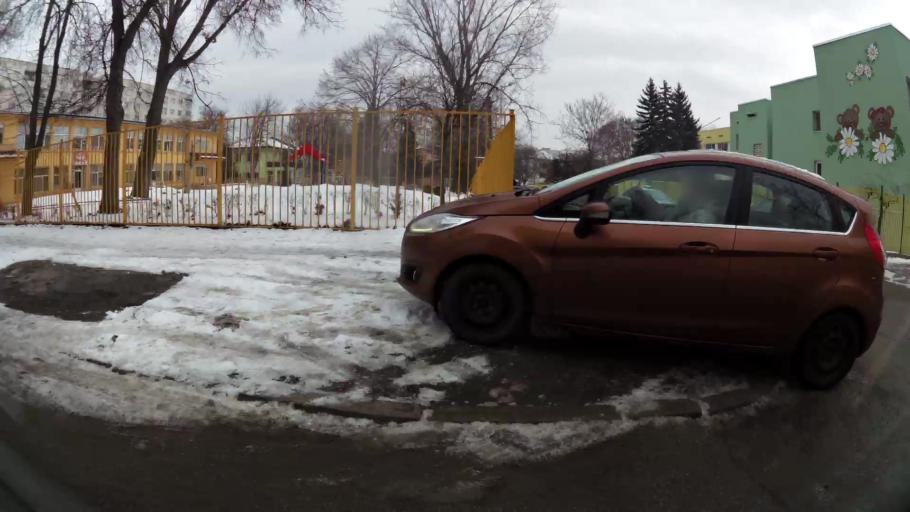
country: BG
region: Sofia-Capital
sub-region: Stolichna Obshtina
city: Sofia
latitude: 42.7143
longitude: 23.3001
